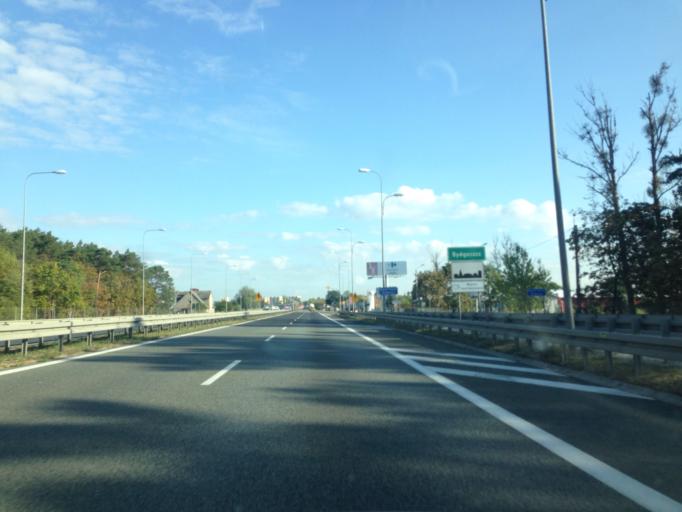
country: PL
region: Kujawsko-Pomorskie
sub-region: Bydgoszcz
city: Bydgoszcz
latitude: 53.0940
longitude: 18.0084
